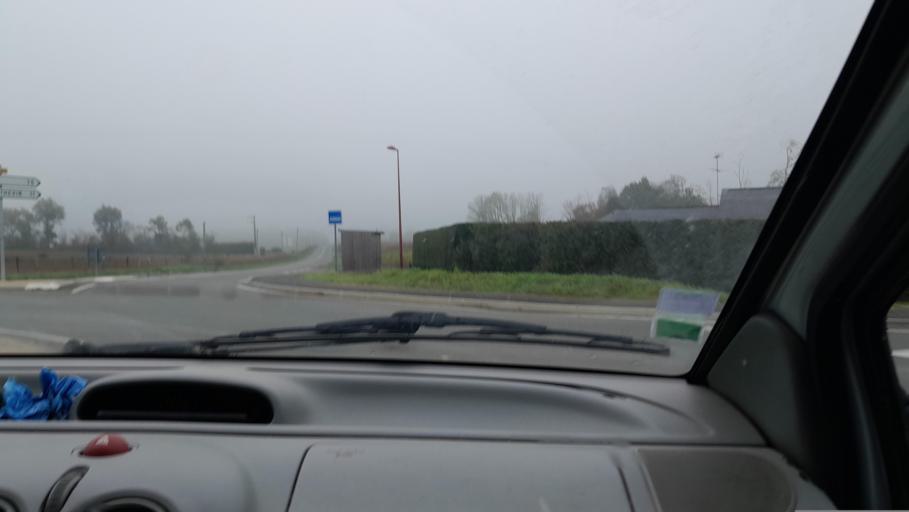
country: FR
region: Pays de la Loire
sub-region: Departement de la Mayenne
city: Loiron
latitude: 48.0170
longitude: -0.9382
